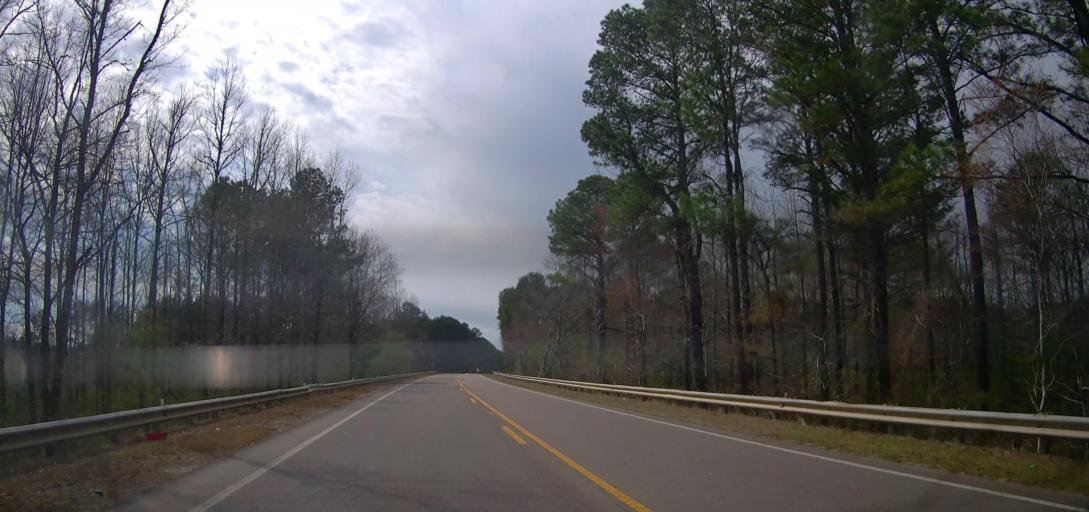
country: US
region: Alabama
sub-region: Walker County
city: Carbon Hill
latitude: 33.8763
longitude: -87.4847
